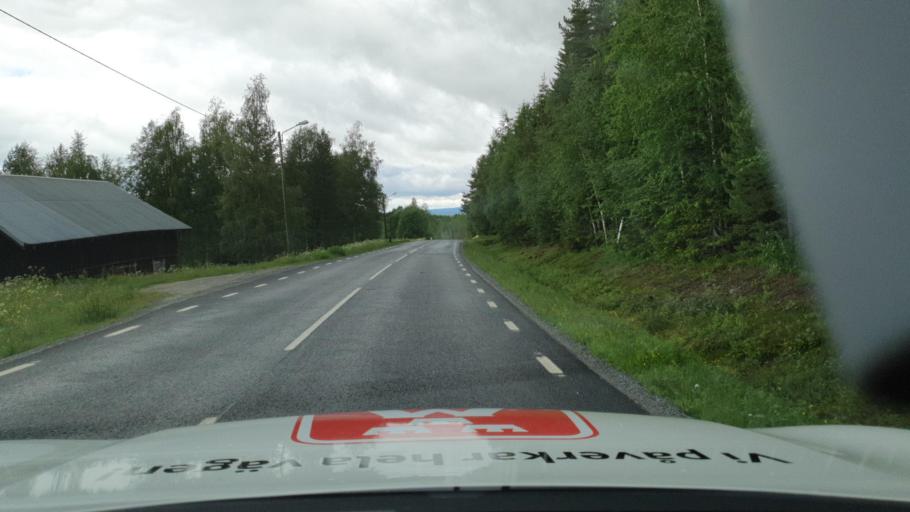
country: SE
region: Vaesterbotten
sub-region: Dorotea Kommun
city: Dorotea
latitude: 64.2406
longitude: 16.5375
